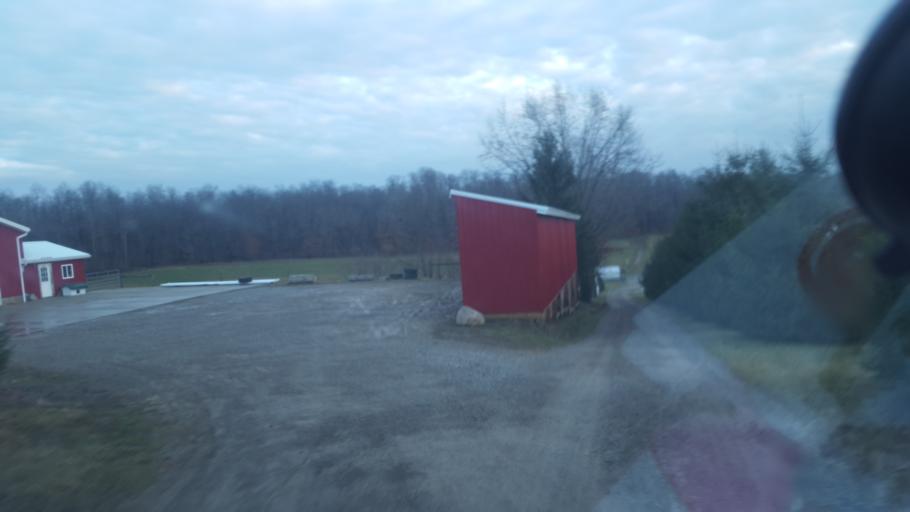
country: US
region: Ohio
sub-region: Knox County
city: Danville
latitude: 40.5334
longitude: -82.3545
